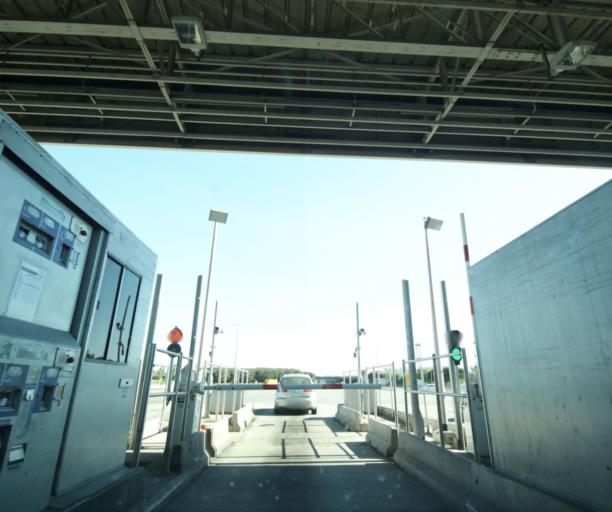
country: FR
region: Midi-Pyrenees
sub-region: Departement de la Haute-Garonne
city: Aucamville
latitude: 43.6580
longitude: 1.4269
